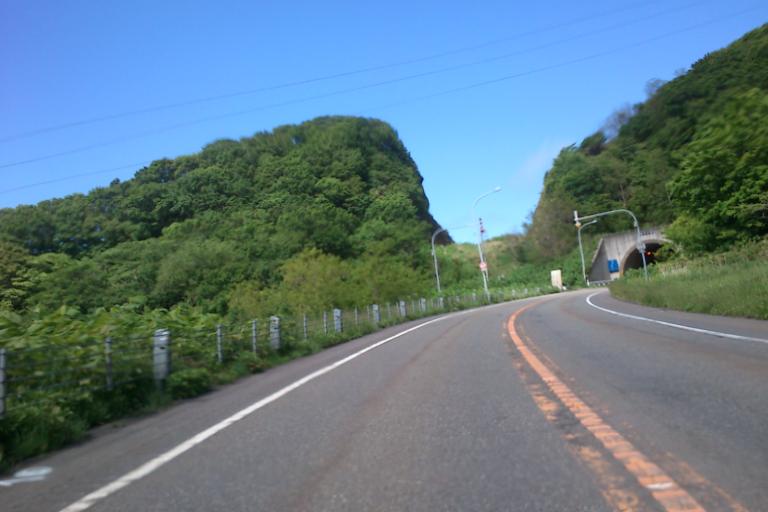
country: JP
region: Hokkaido
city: Ishikari
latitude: 43.4805
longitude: 141.3923
